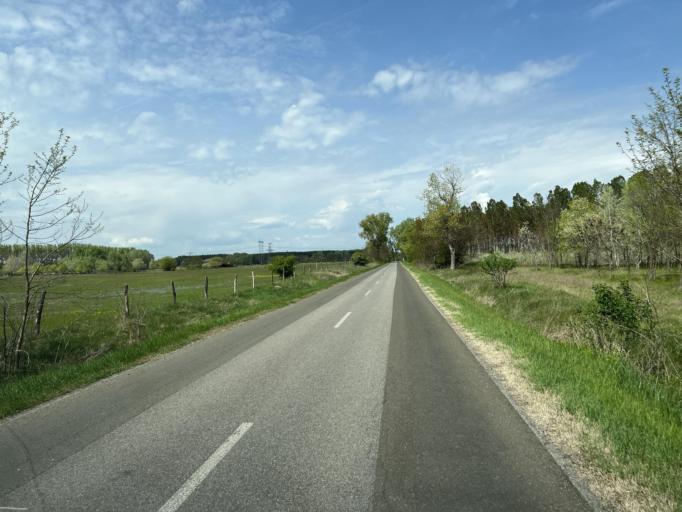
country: HU
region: Pest
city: Albertirsa
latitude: 47.1979
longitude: 19.6117
